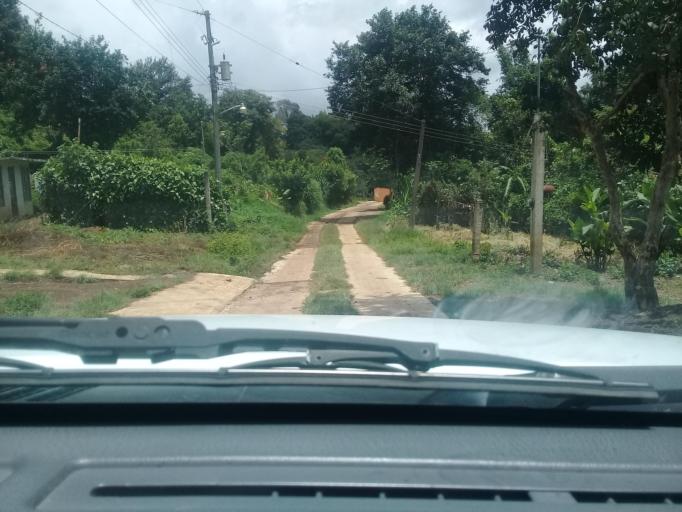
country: MX
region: Veracruz
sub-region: Tlalnelhuayocan
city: Otilpan
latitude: 19.5439
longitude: -96.9772
